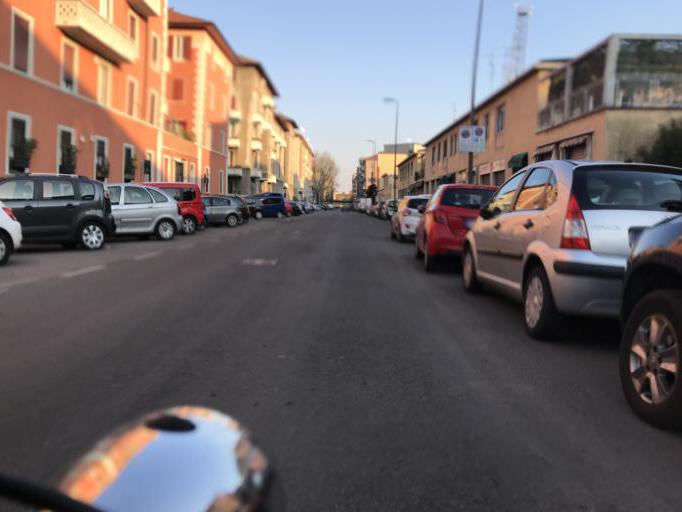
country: IT
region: Lombardy
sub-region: Citta metropolitana di Milano
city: Novate Milanese
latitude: 45.4962
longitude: 9.1504
